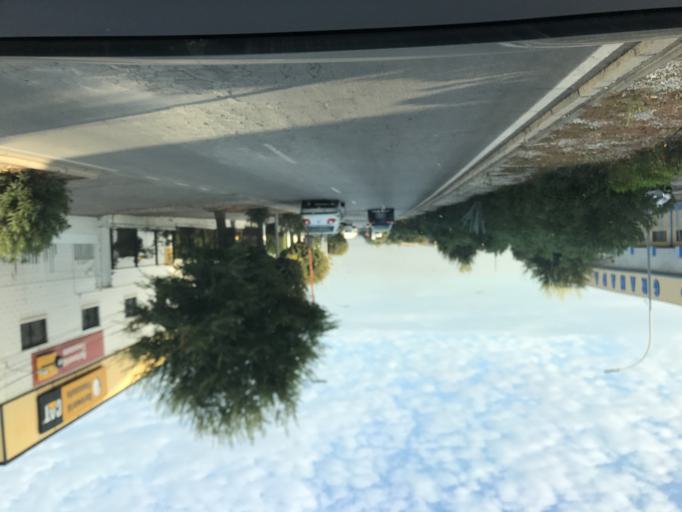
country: ES
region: Andalusia
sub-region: Provincia de Granada
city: Peligros
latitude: 37.2259
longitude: -3.6414
